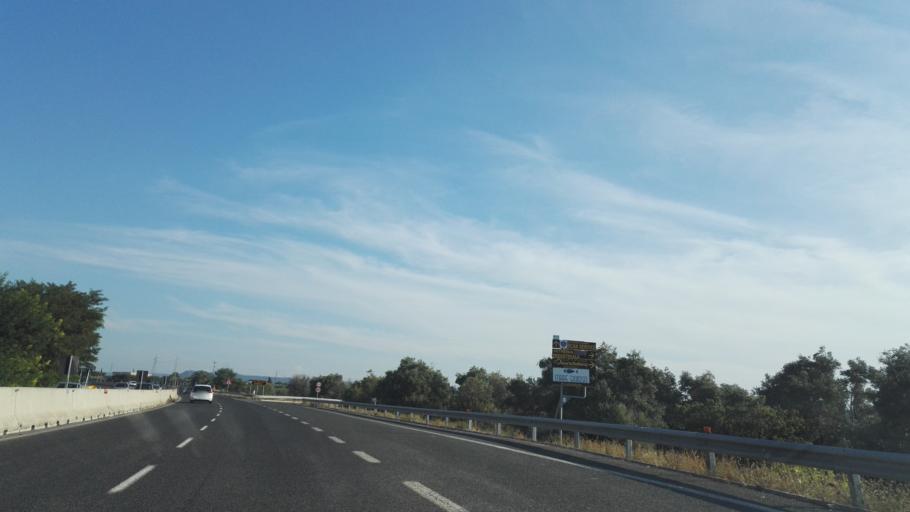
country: IT
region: Apulia
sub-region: Provincia di Bari
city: Monopoli
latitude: 40.9555
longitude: 17.2600
